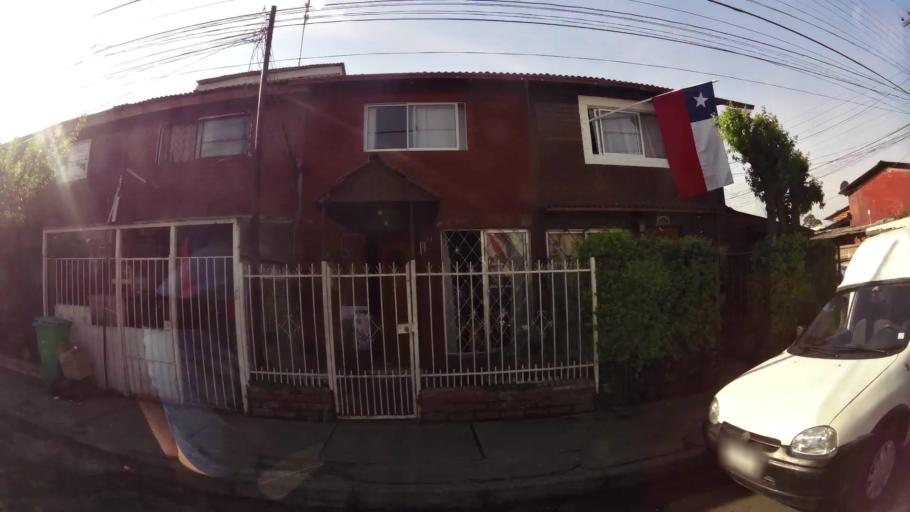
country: CL
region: Santiago Metropolitan
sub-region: Provincia de Santiago
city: Santiago
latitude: -33.5097
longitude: -70.6345
